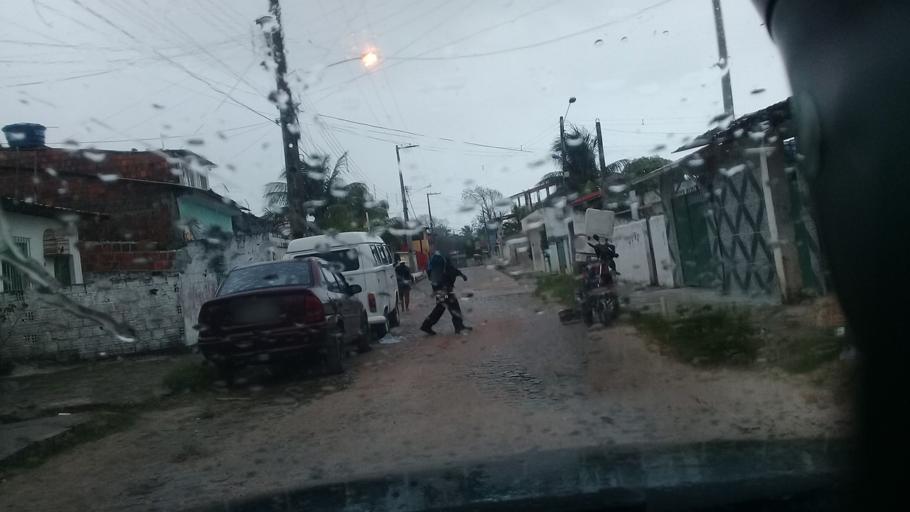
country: BR
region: Pernambuco
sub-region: Itamaraca
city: Itamaraca
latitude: -7.7457
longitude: -34.8276
